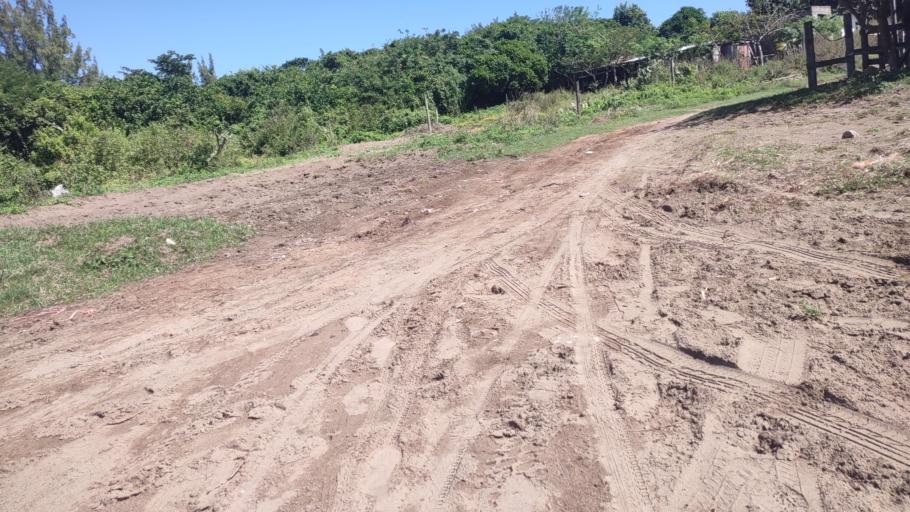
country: MX
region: Veracruz
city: Heroica Alvarado
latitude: 18.7863
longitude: -95.7694
